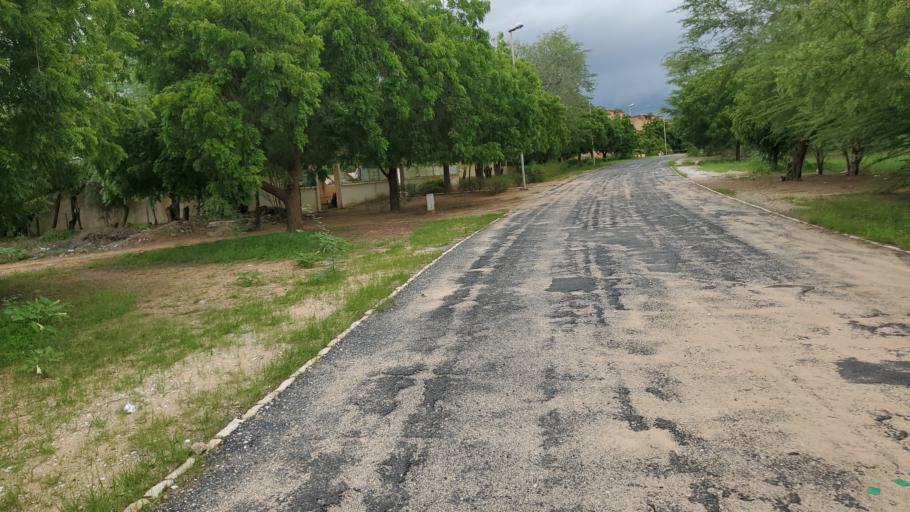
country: SN
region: Saint-Louis
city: Saint-Louis
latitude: 16.0687
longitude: -16.4184
